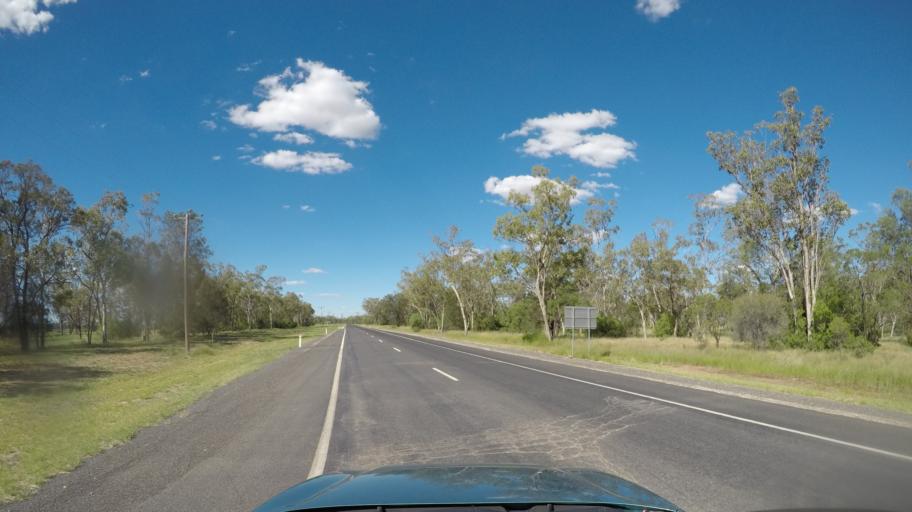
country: AU
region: Queensland
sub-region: Goondiwindi
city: Goondiwindi
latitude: -28.1781
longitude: 150.2818
